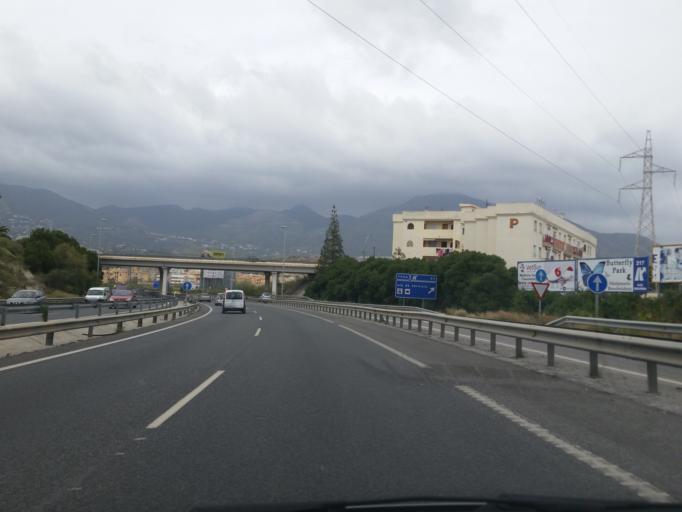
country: ES
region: Andalusia
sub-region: Provincia de Malaga
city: Fuengirola
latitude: 36.5570
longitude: -4.6201
